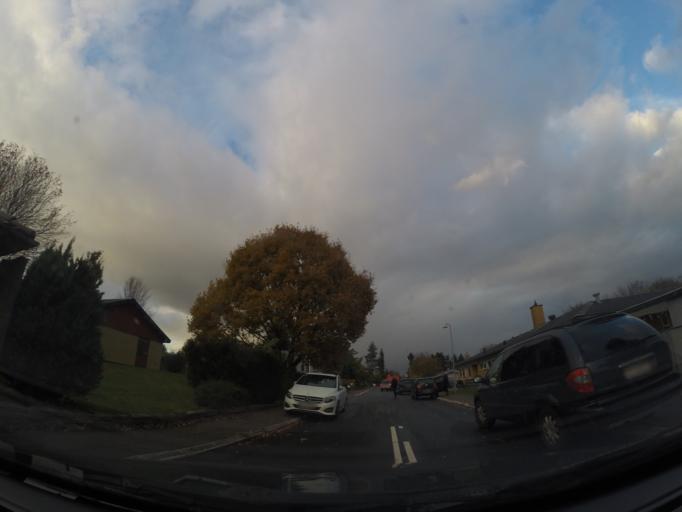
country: DK
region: Capital Region
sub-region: Hoje-Taastrup Kommune
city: Taastrup
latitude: 55.6816
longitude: 12.2437
